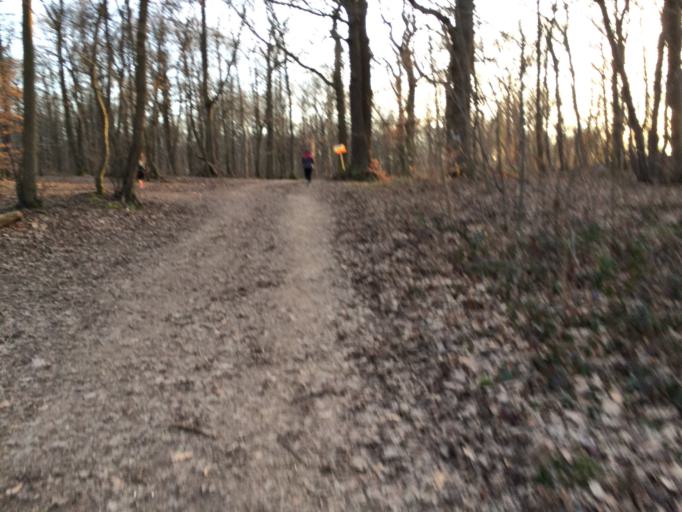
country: FR
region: Ile-de-France
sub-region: Departement des Hauts-de-Seine
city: Meudon
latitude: 48.8038
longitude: 2.2485
